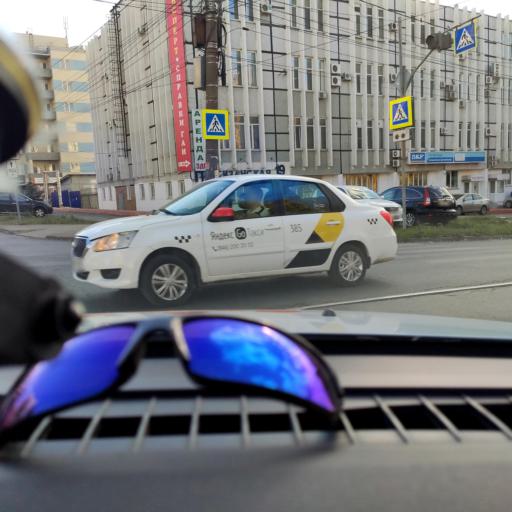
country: RU
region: Samara
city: Samara
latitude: 53.1911
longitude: 50.1719
